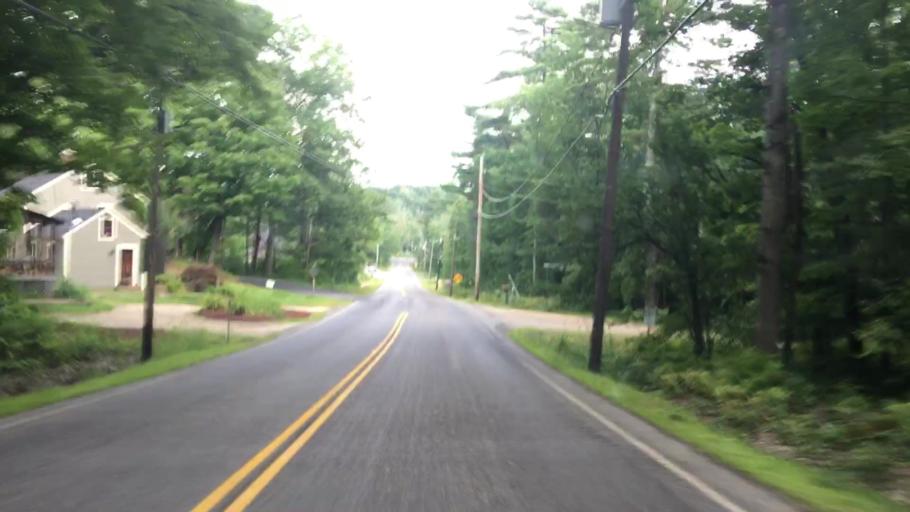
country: US
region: New Hampshire
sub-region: Belknap County
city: Sanbornton
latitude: 43.4932
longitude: -71.5883
